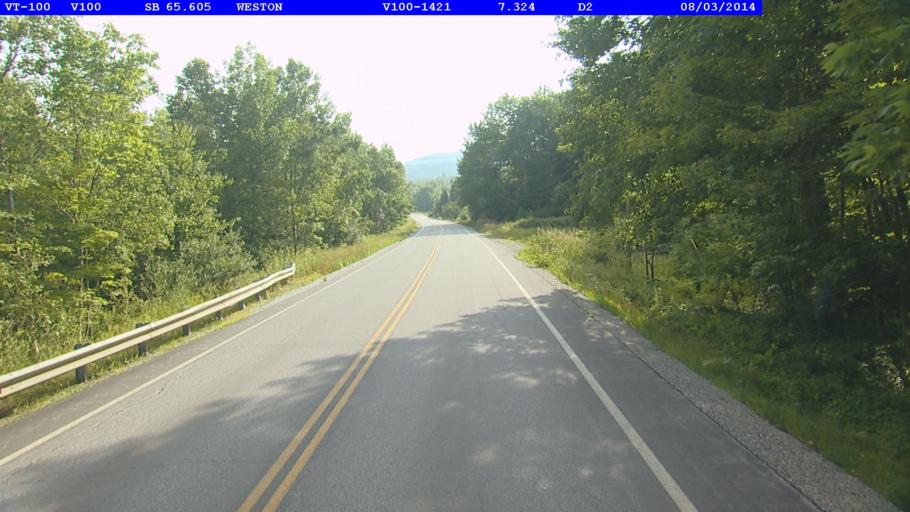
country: US
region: Vermont
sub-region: Windsor County
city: Chester
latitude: 43.3452
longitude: -72.7772
